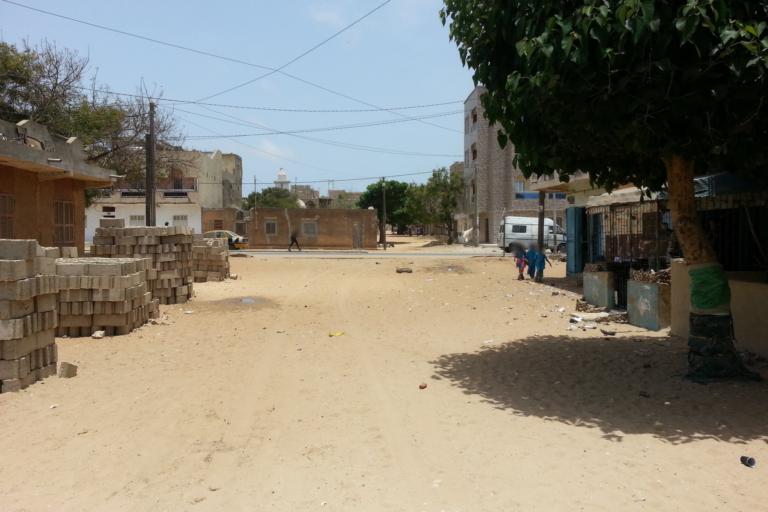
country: SN
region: Dakar
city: Pikine
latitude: 14.7830
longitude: -17.3735
